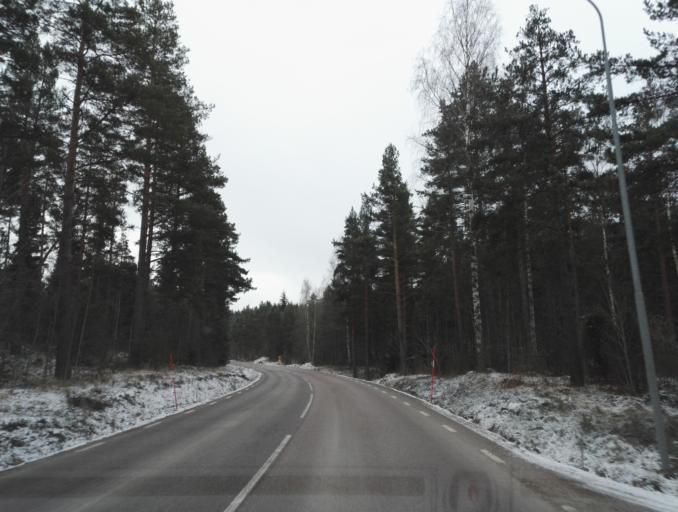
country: SE
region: Kalmar
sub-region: Hultsfreds Kommun
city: Virserum
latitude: 57.3990
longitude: 15.6030
